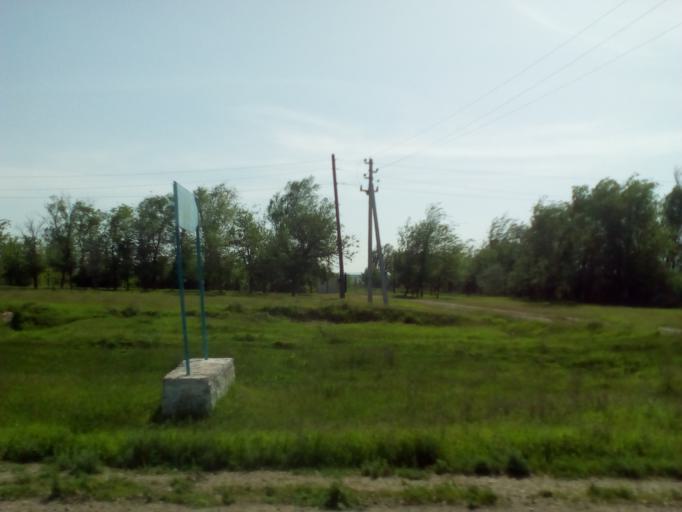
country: KZ
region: Ongtustik Qazaqstan
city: Shayan
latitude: 43.0539
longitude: 69.3906
